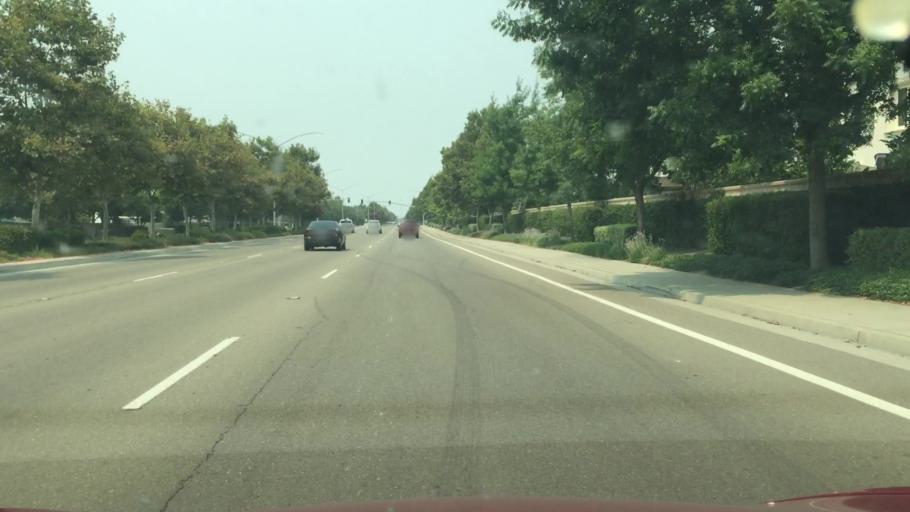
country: US
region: California
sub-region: San Joaquin County
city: Morada
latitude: 38.0292
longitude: -121.2695
